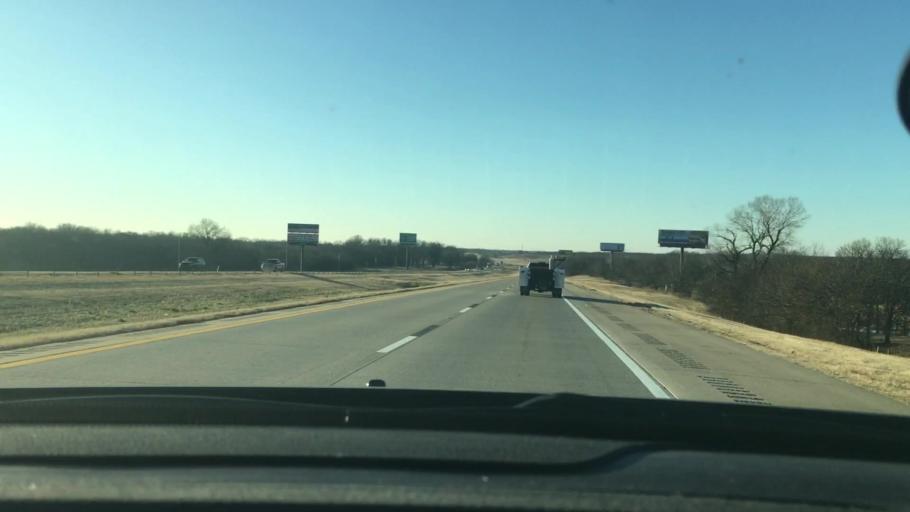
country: US
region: Oklahoma
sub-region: Carter County
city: Ardmore
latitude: 34.2731
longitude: -97.1624
